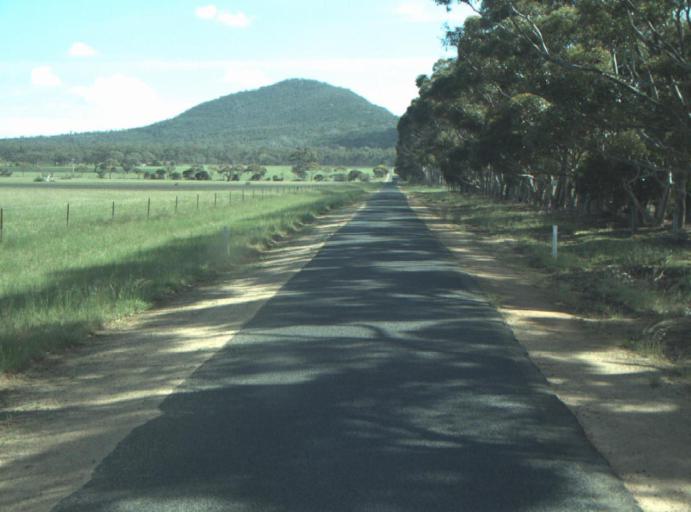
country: AU
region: Victoria
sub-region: Greater Geelong
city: Lara
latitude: -37.9794
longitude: 144.4229
